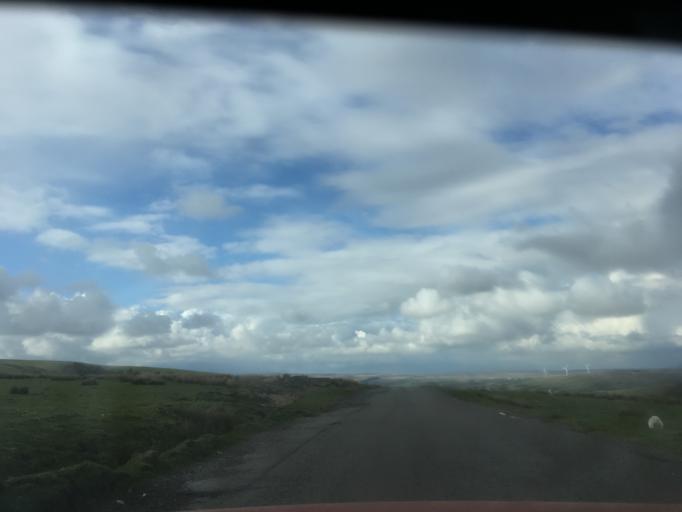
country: GB
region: Wales
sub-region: Caerphilly County Borough
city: Rhymney
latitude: 51.7268
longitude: -3.2972
